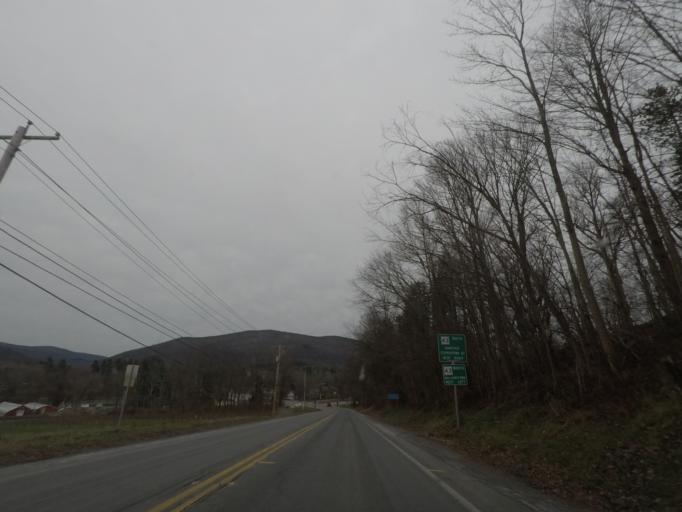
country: US
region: Massachusetts
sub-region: Berkshire County
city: Williamstown
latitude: 42.6625
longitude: -73.2409
